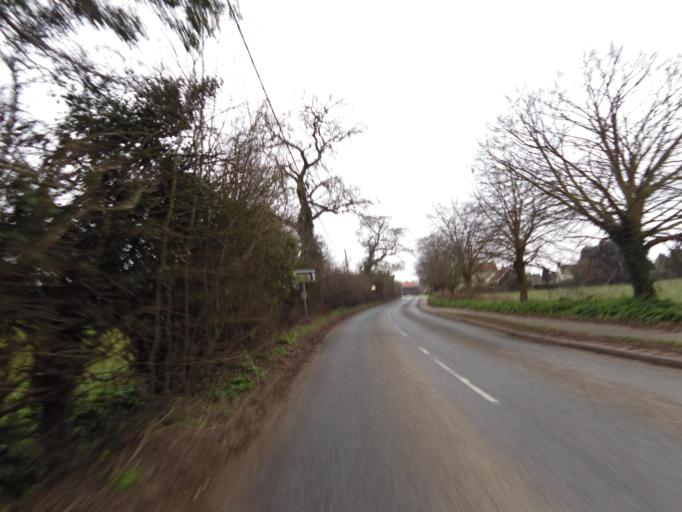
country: GB
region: England
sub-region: Suffolk
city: Wickham Market
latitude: 52.1517
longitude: 1.3963
